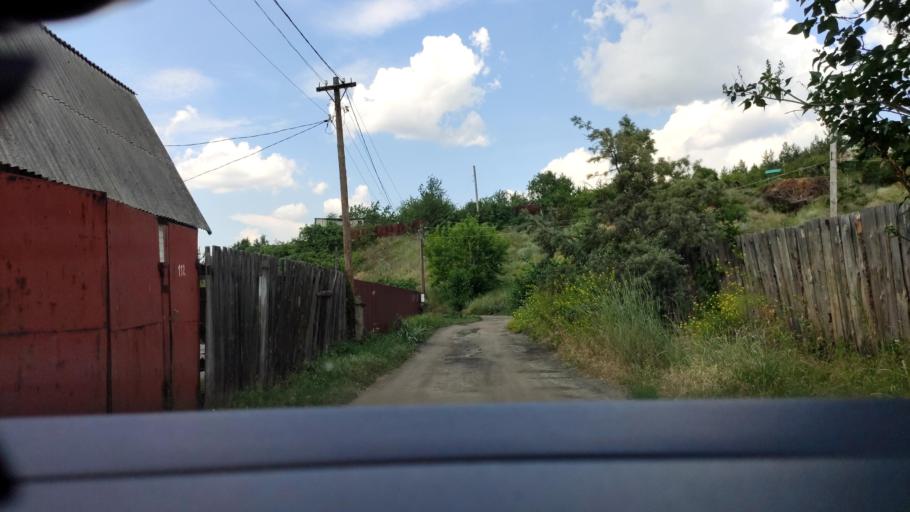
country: RU
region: Voronezj
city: Maslovka
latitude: 51.6096
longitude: 39.2872
